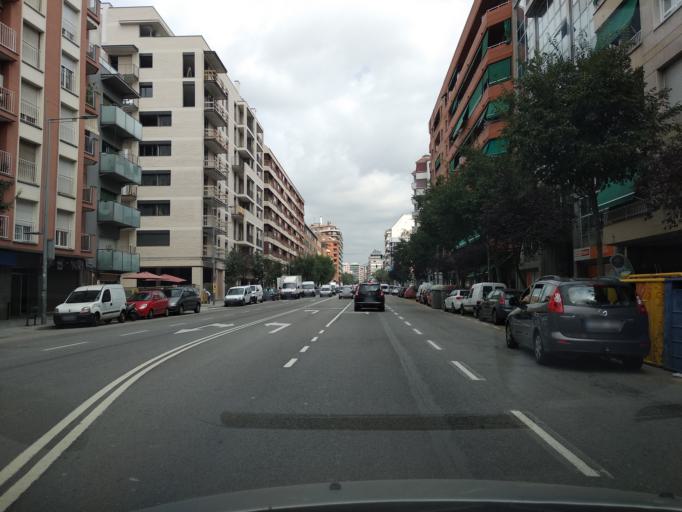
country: ES
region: Catalonia
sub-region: Provincia de Barcelona
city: Granollers
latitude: 41.6032
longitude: 2.2904
